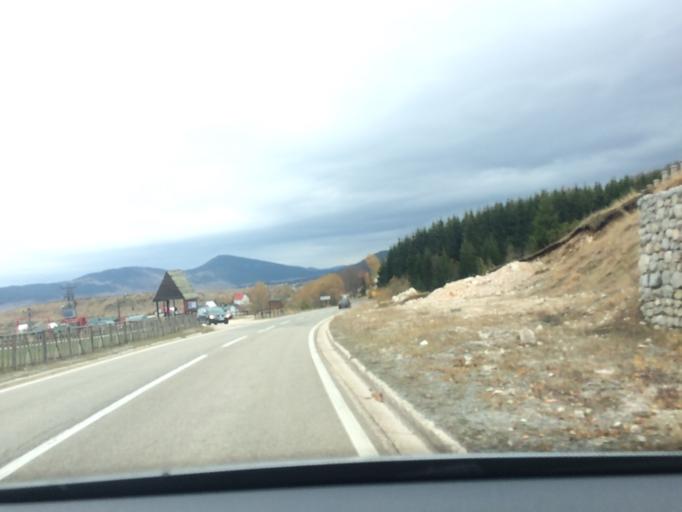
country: ME
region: Opstina Zabljak
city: Zabljak
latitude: 43.1631
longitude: 19.1401
